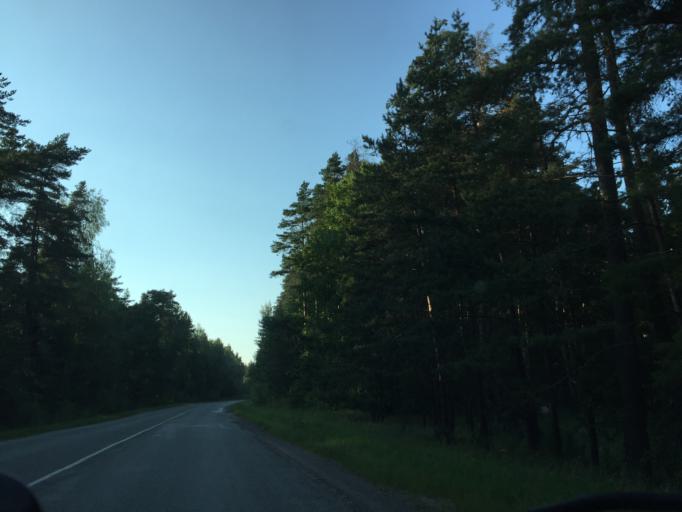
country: LV
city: Tervete
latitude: 56.4576
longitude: 23.4074
